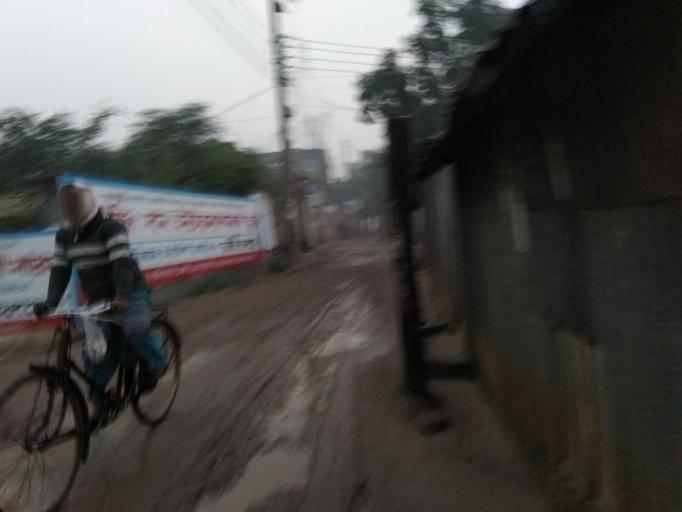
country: BD
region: Dhaka
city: Tungi
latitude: 23.8576
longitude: 90.4305
